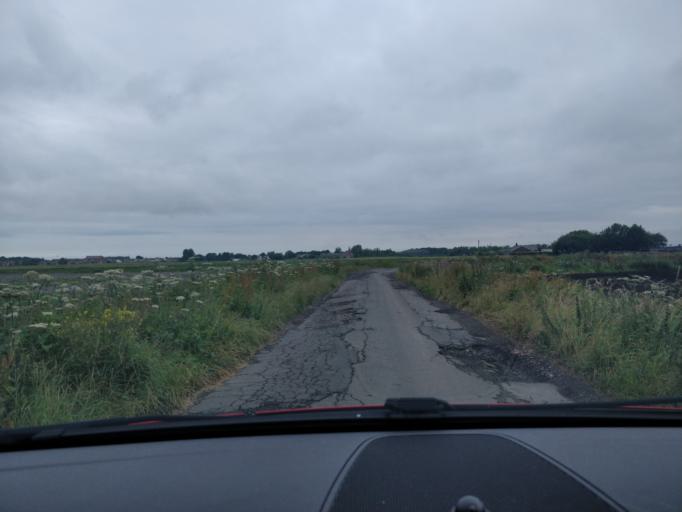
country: GB
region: England
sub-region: Lancashire
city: Banks
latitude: 53.6636
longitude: -2.9353
